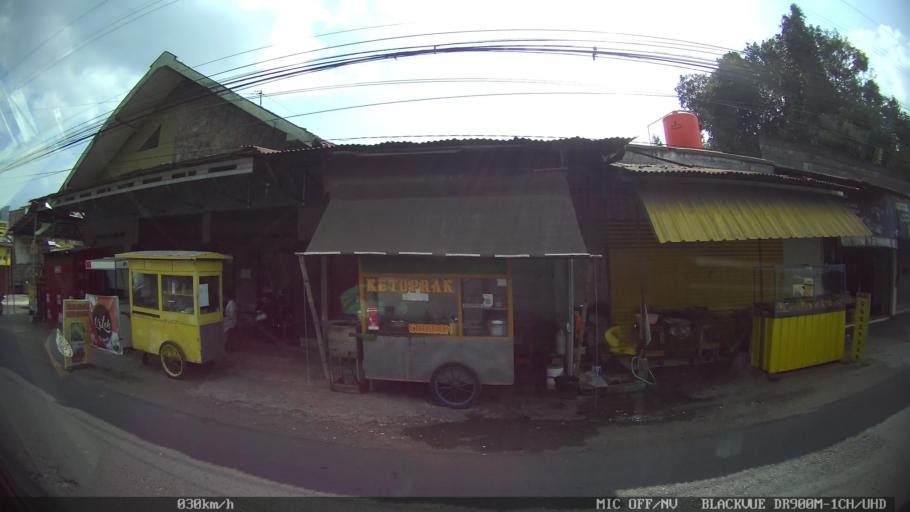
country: ID
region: Daerah Istimewa Yogyakarta
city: Kasihan
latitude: -7.8237
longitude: 110.3282
